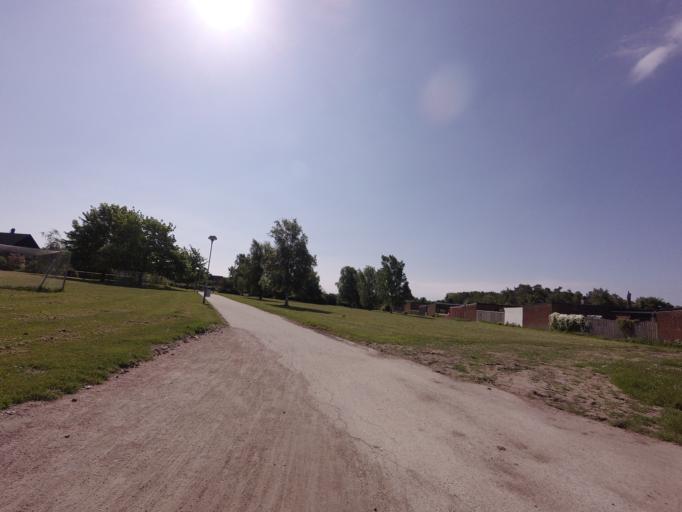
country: SE
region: Skane
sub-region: Vellinge Kommun
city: Hollviken
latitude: 55.4246
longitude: 12.9679
